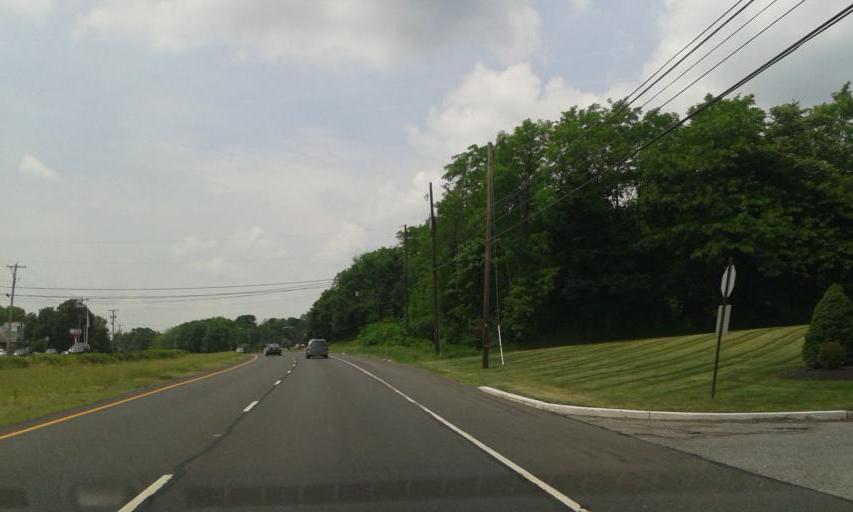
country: US
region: New Jersey
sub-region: Hunterdon County
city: Whitehouse Station
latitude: 40.6397
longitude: -74.7942
